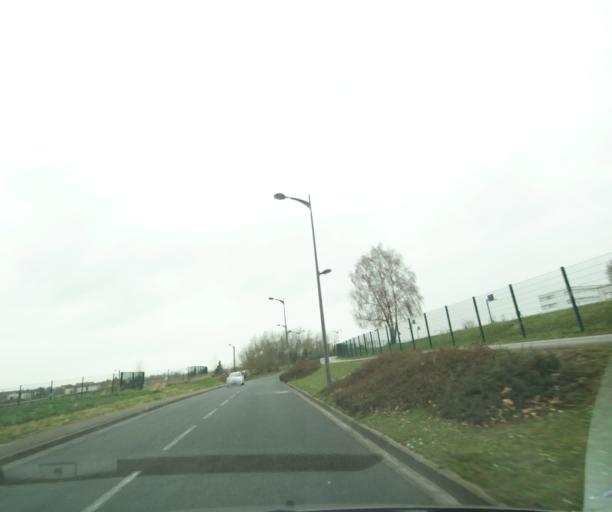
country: FR
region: Picardie
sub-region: Departement de l'Oise
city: Noyon
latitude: 49.5845
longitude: 3.0135
